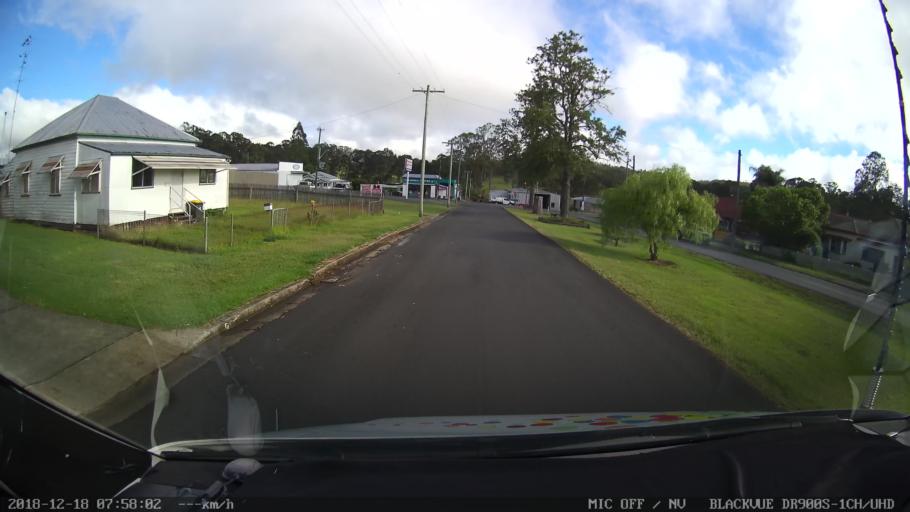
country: AU
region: New South Wales
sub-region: Kyogle
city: Kyogle
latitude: -28.3899
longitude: 152.6122
